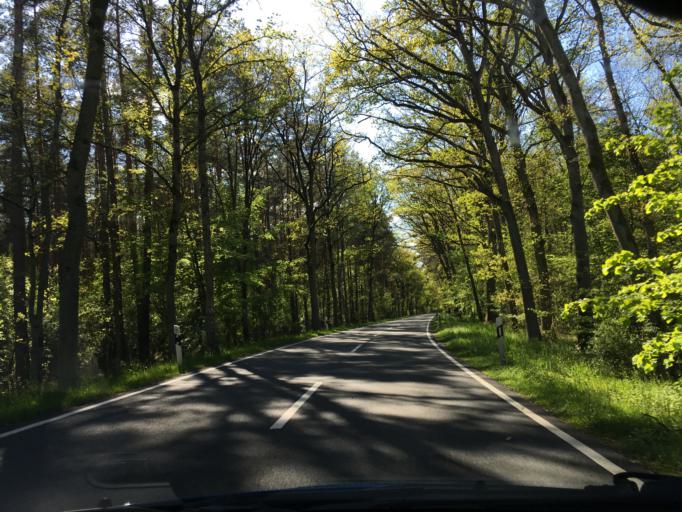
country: DE
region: Lower Saxony
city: Gartow
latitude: 53.0163
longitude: 11.5197
